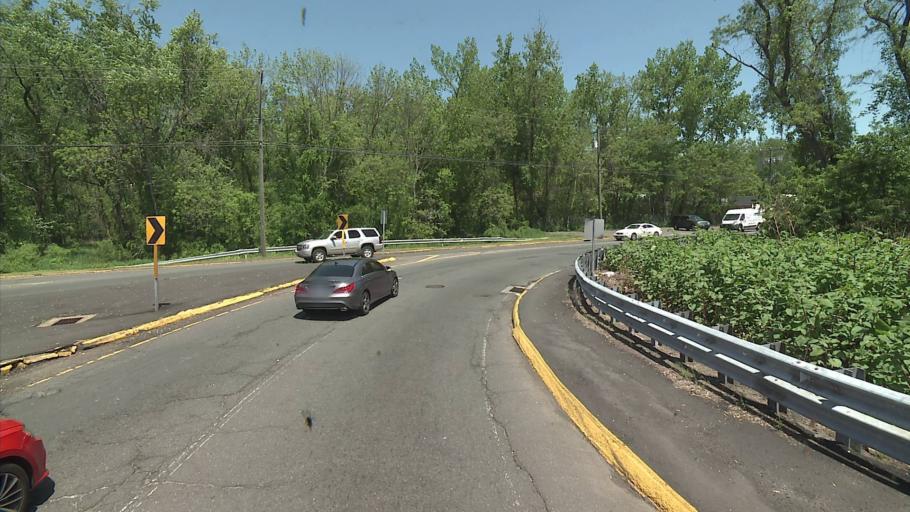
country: US
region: Connecticut
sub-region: Hartford County
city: Hartford
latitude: 41.7708
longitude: -72.6515
